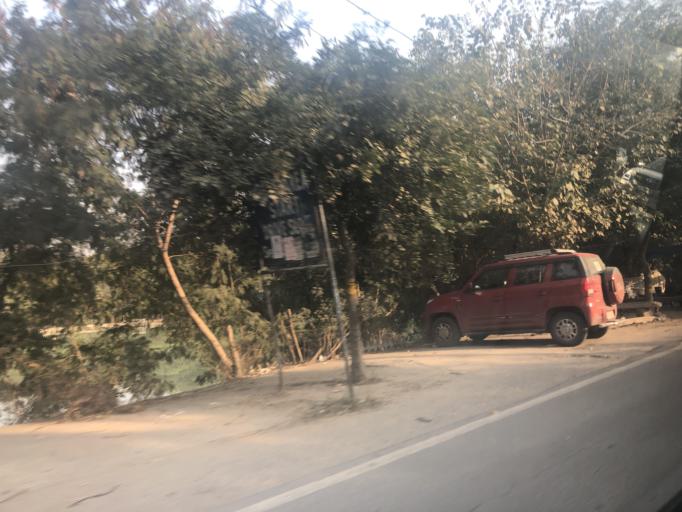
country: IN
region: Haryana
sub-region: Gurgaon
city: Gurgaon
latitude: 28.5556
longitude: 77.0058
